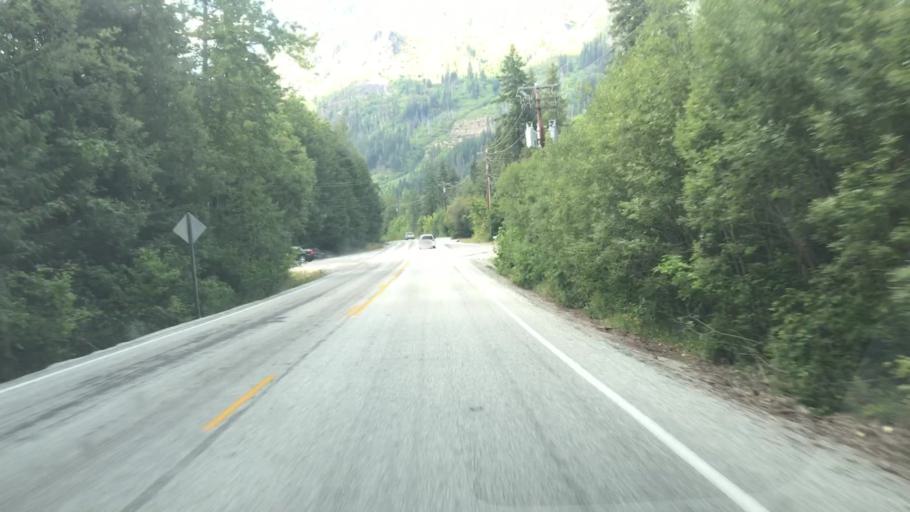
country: US
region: Washington
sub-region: Chelan County
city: Leavenworth
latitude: 47.8314
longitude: -120.7743
